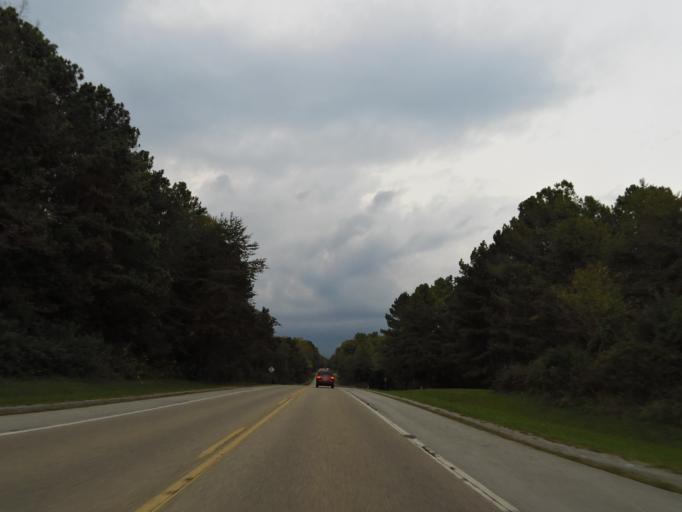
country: US
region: Tennessee
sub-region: Loudon County
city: Loudon
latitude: 35.7061
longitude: -84.2626
